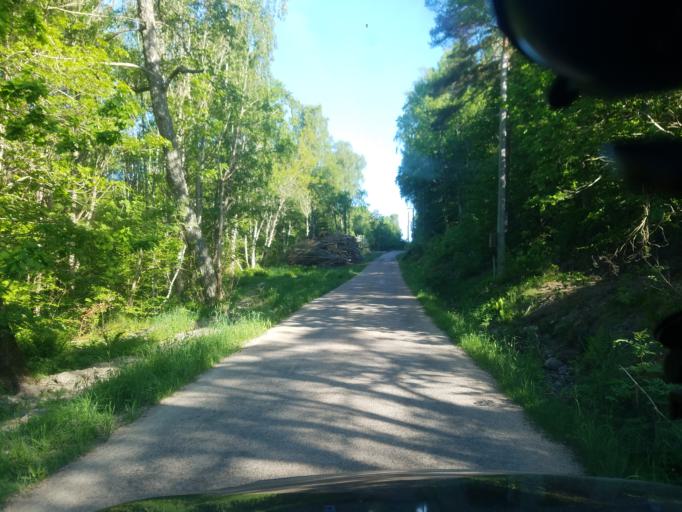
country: SE
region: Vaestra Goetaland
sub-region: Orust
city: Henan
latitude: 58.2791
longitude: 11.6395
